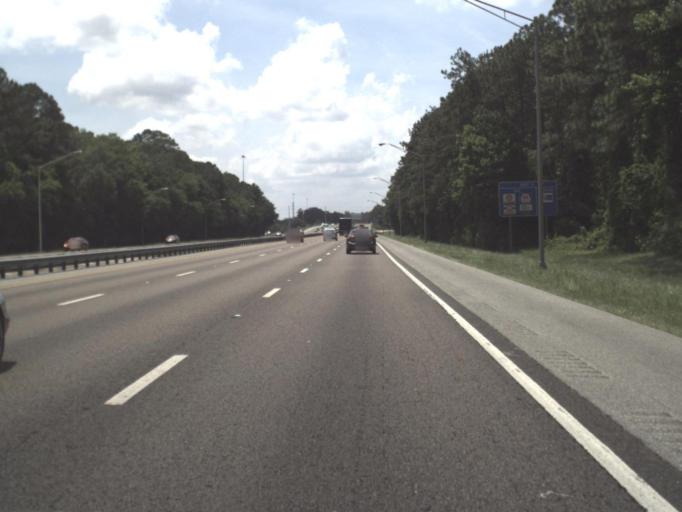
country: US
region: Florida
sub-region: Saint Johns County
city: Fruit Cove
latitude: 30.1687
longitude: -81.5934
